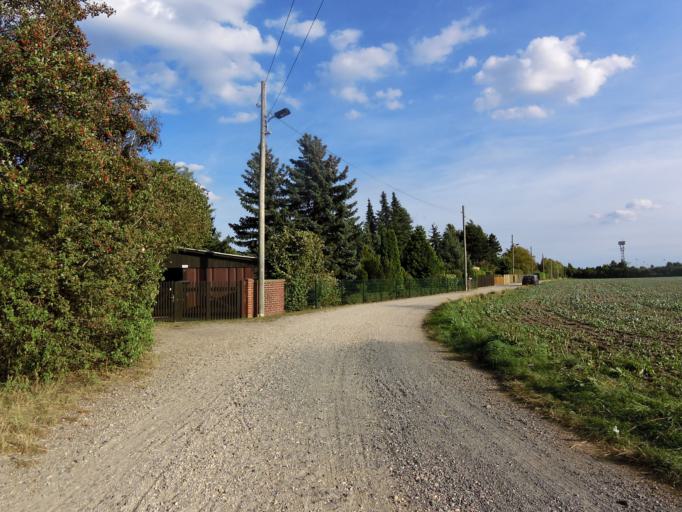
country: DE
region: Saxony
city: Schkeuditz
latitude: 51.3518
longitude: 12.2676
